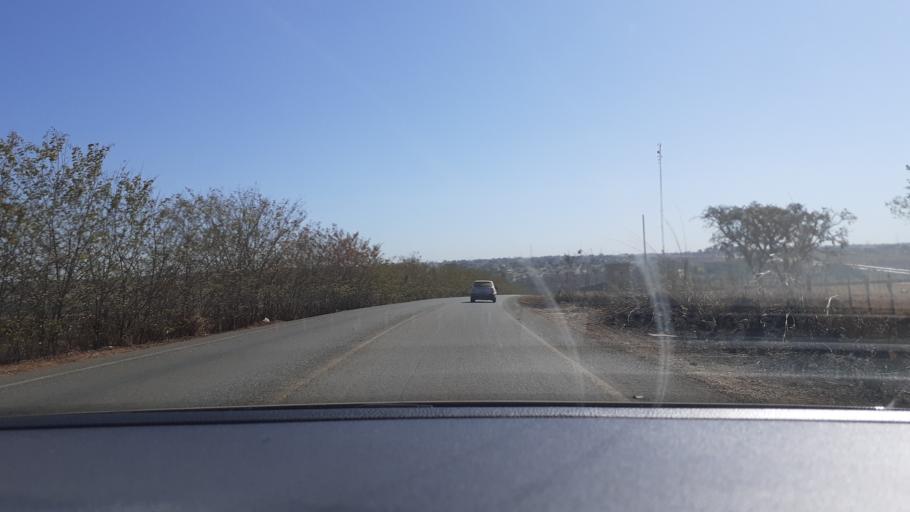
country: BR
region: Goias
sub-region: Aparecida De Goiania
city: Aparecida de Goiania
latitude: -16.8575
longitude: -49.2566
